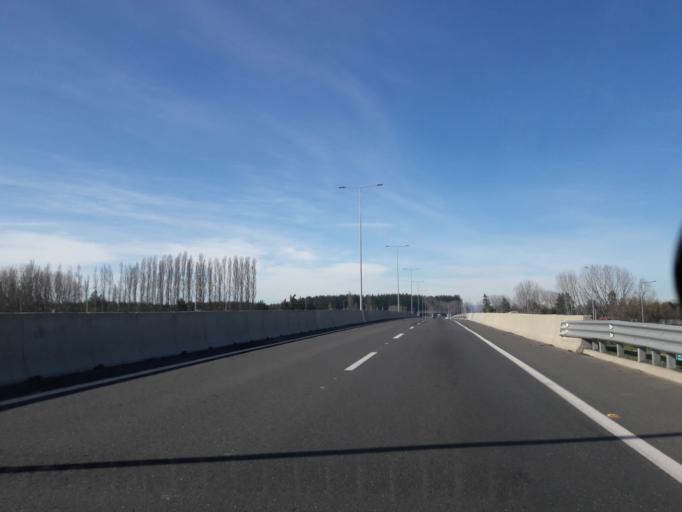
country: CL
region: Biobio
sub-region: Provincia de Biobio
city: Cabrero
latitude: -37.0305
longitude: -72.4301
